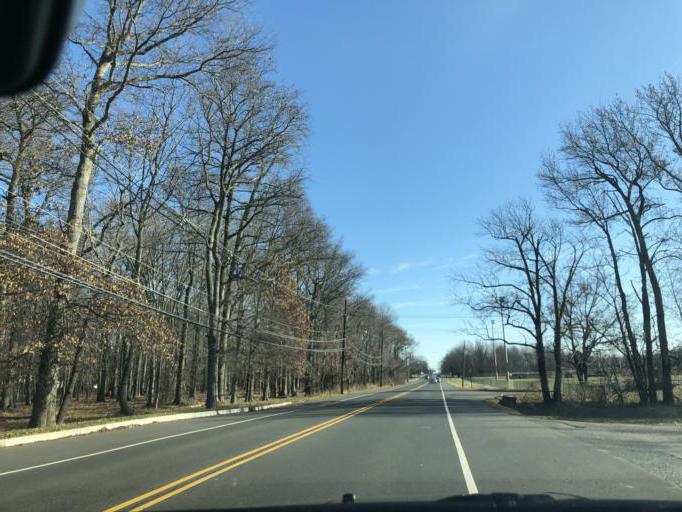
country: US
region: New Jersey
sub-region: Burlington County
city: Cinnaminson
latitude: 39.9771
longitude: -74.9859
